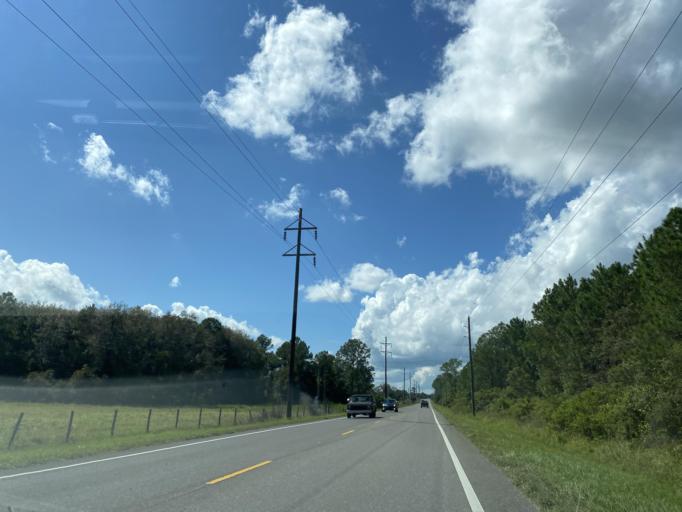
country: US
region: Florida
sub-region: Lake County
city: Umatilla
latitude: 28.9603
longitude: -81.6163
